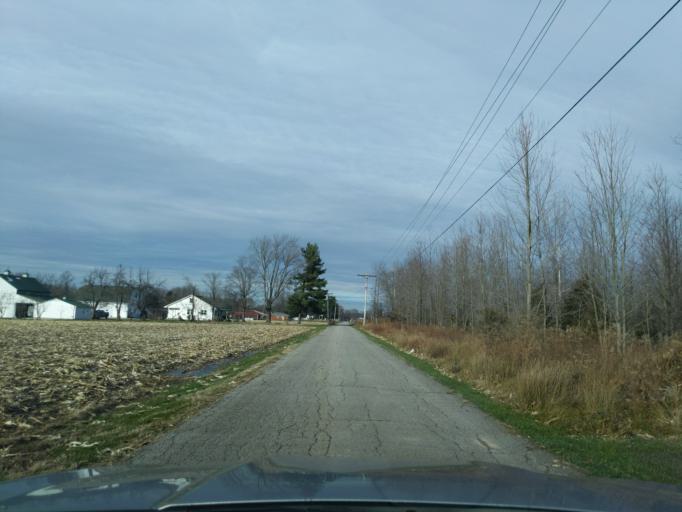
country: US
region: Indiana
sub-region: Decatur County
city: Greensburg
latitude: 39.2040
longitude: -85.4329
